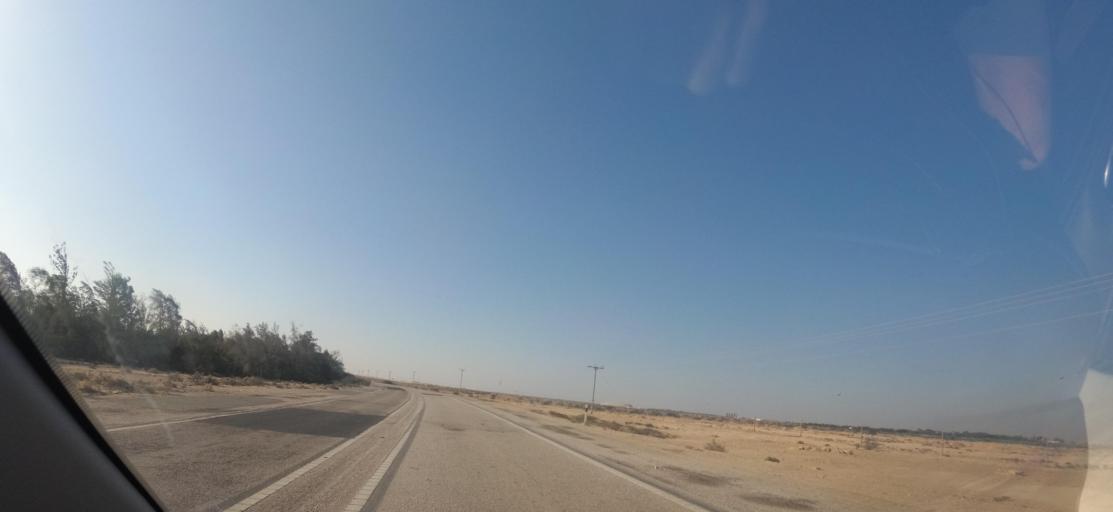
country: QA
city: Al Ghuwayriyah
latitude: 25.8556
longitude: 51.2560
